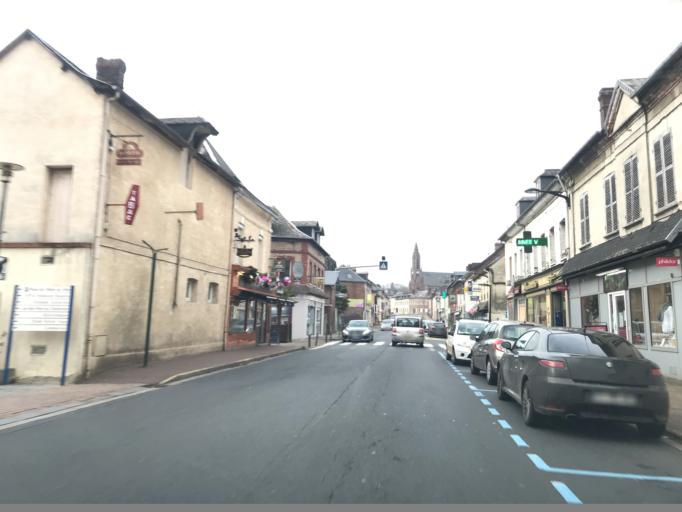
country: FR
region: Haute-Normandie
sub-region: Departement de l'Eure
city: Fleury-sur-Andelle
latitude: 49.3607
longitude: 1.3570
